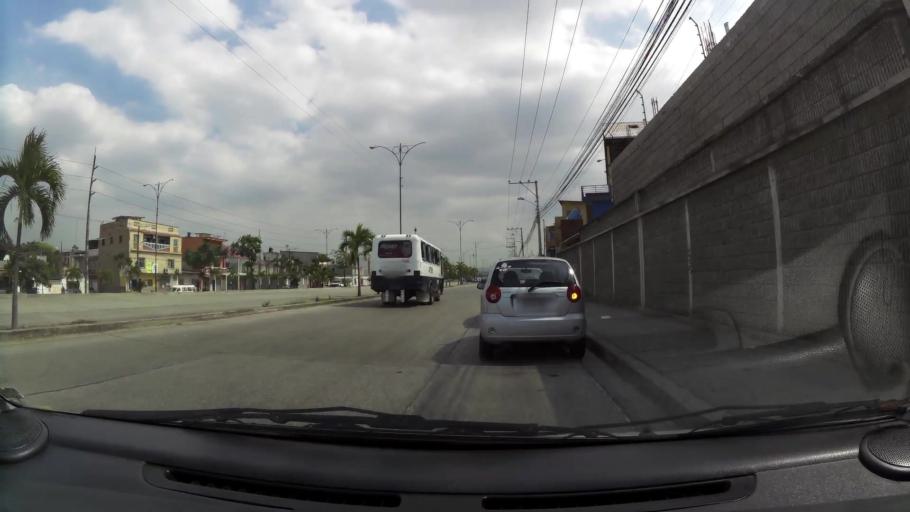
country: EC
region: Guayas
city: Eloy Alfaro
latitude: -2.0837
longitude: -79.9182
